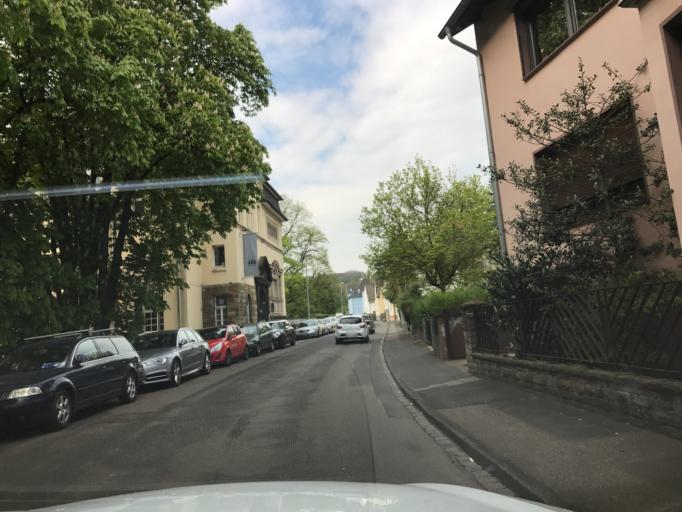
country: DE
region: North Rhine-Westphalia
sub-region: Regierungsbezirk Koln
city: Konigswinter
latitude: 50.6756
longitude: 7.1972
